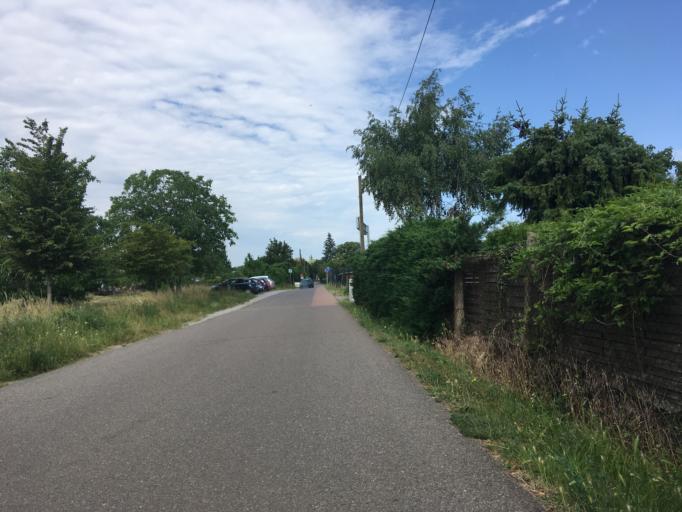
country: DE
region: Saxony-Anhalt
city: Bernburg
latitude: 51.7879
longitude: 11.7604
